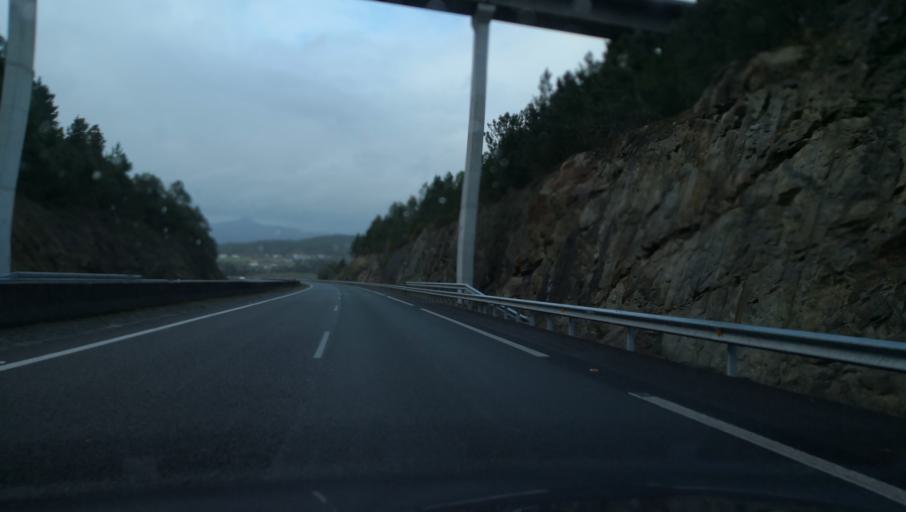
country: ES
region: Galicia
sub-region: Provincia da Coruna
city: Ribeira
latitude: 42.7401
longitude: -8.3702
